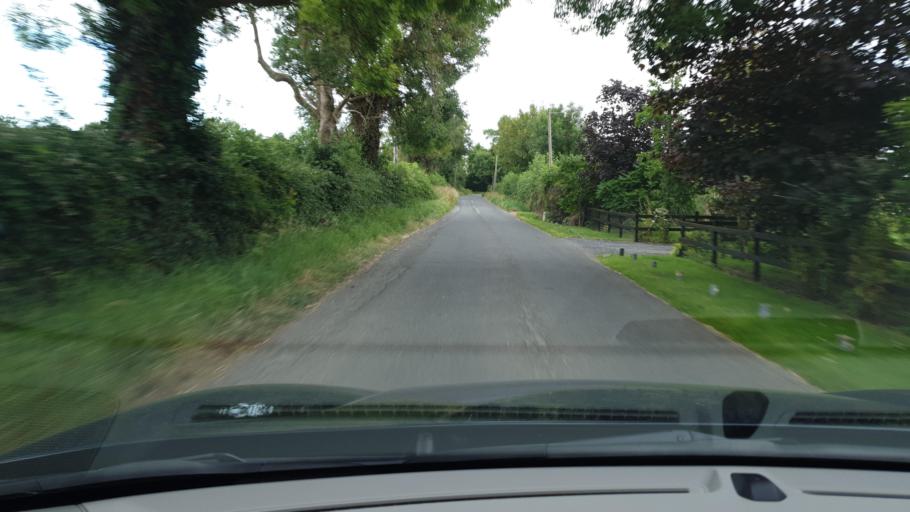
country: IE
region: Leinster
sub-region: An Mhi
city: Stamullin
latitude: 53.5863
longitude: -6.3246
